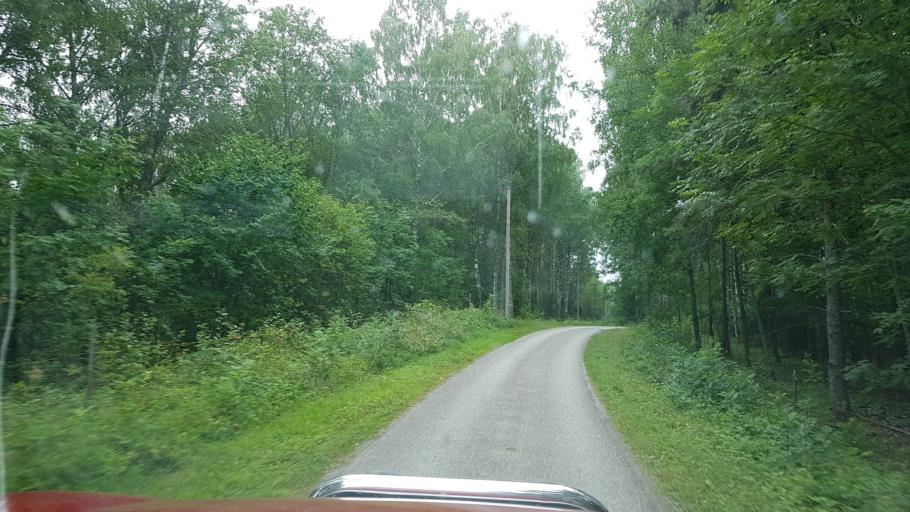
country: EE
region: Laeaene
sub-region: Ridala Parish
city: Uuemoisa
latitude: 58.9987
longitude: 23.6454
